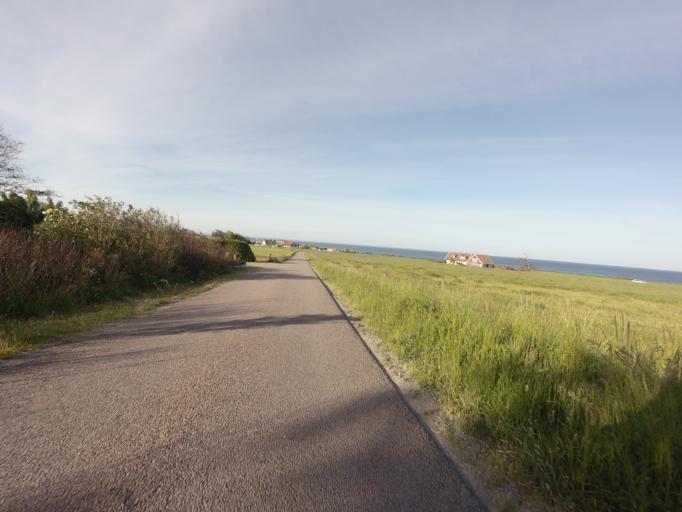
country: SE
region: Skane
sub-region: Hoganas Kommun
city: Hoganas
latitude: 56.2545
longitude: 12.5363
